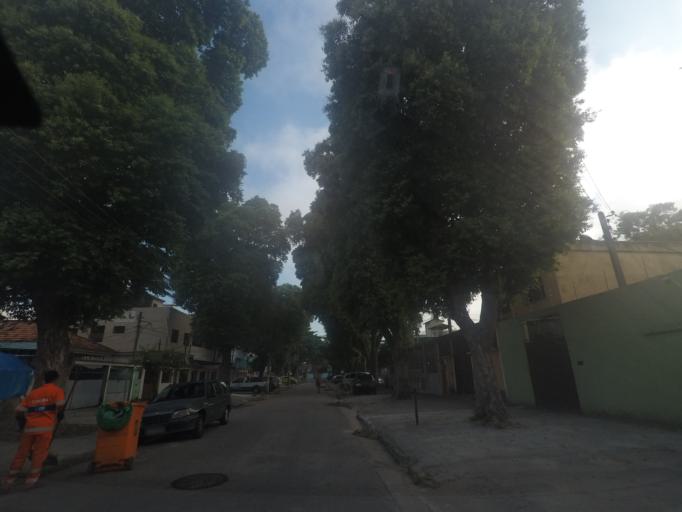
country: BR
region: Rio de Janeiro
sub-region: Duque De Caxias
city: Duque de Caxias
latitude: -22.8359
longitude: -43.2706
